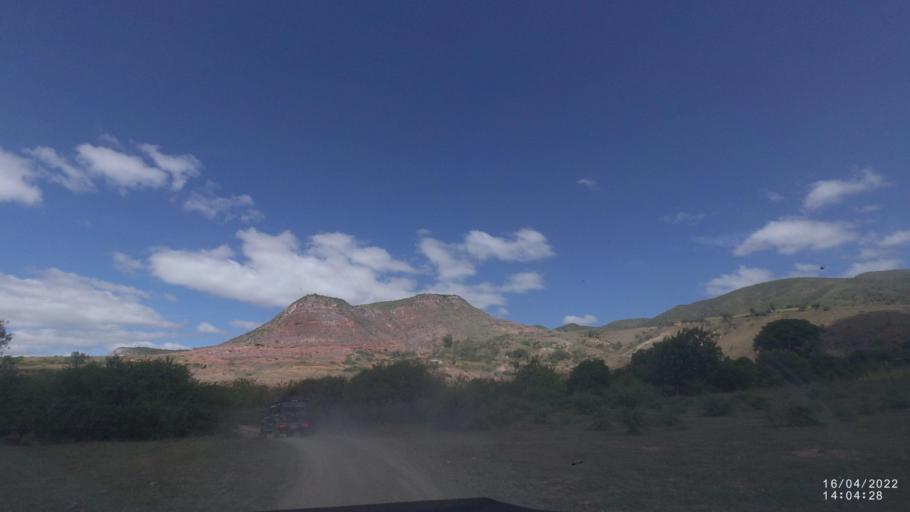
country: BO
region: Cochabamba
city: Mizque
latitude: -18.0561
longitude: -65.5405
